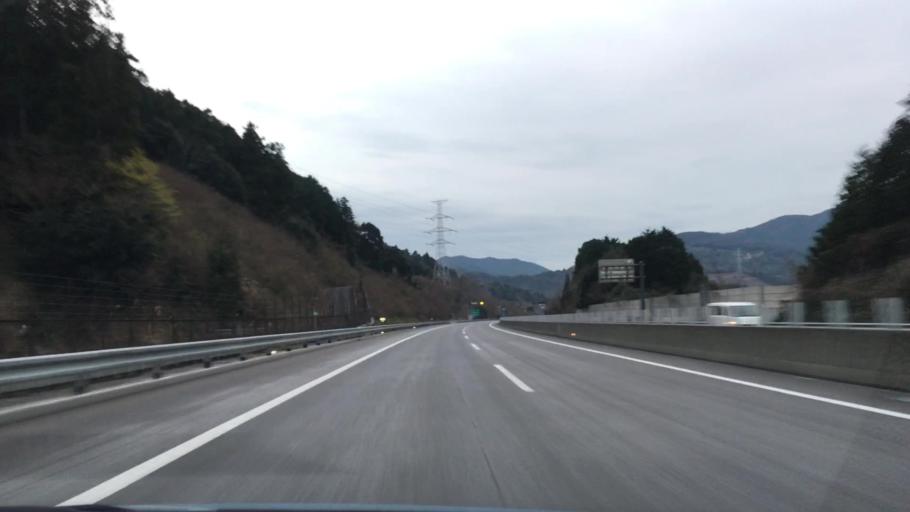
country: JP
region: Aichi
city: Shinshiro
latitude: 34.8651
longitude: 137.6340
